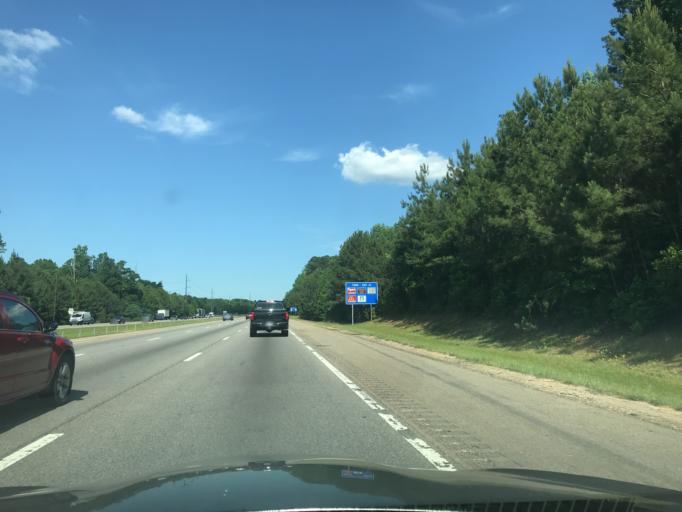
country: US
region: North Carolina
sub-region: Wake County
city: West Raleigh
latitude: 35.8996
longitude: -78.6221
